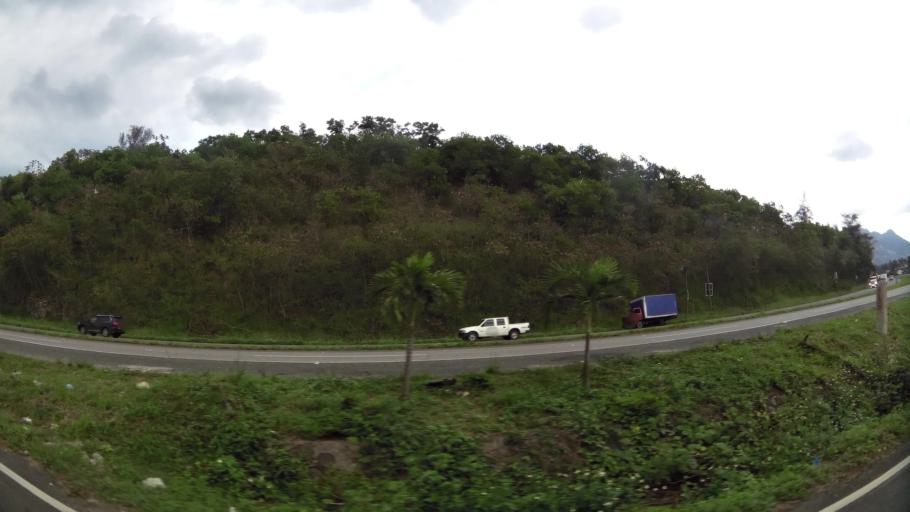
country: DO
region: San Cristobal
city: Villa Altagracia
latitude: 18.6929
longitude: -70.1853
